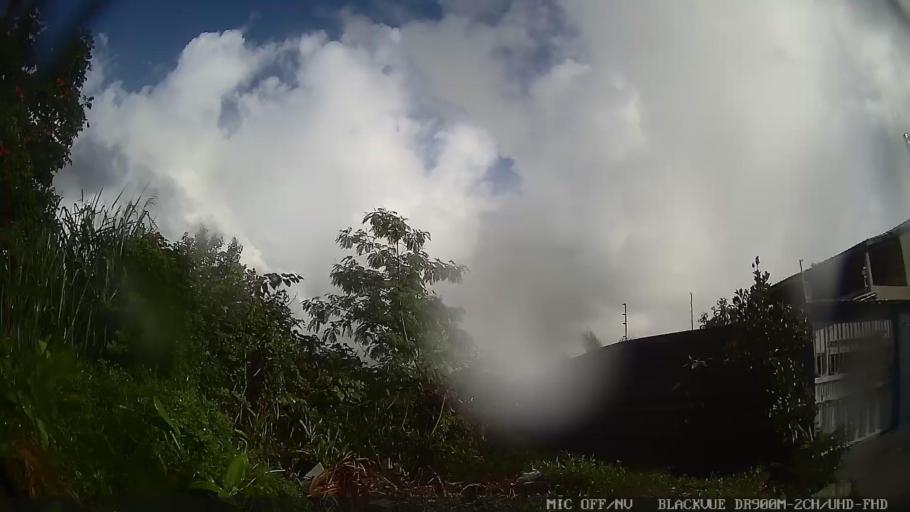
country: BR
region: Sao Paulo
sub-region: Itanhaem
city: Itanhaem
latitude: -24.2404
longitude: -46.8979
